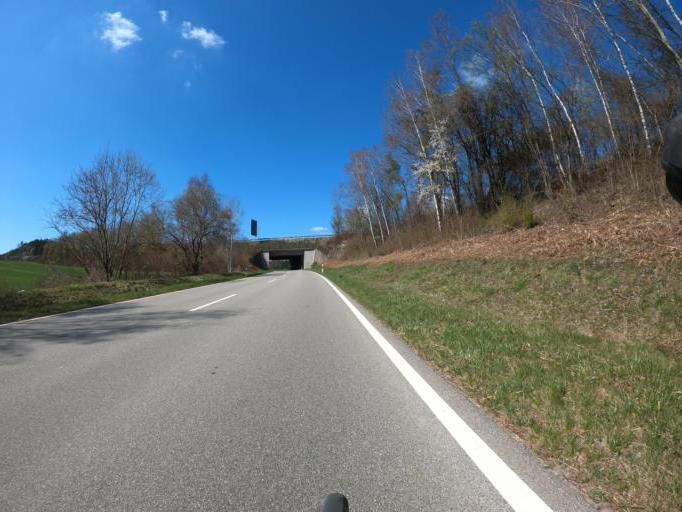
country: DE
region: Baden-Wuerttemberg
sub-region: Karlsruhe Region
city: Empfingen
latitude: 48.4258
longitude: 8.7441
